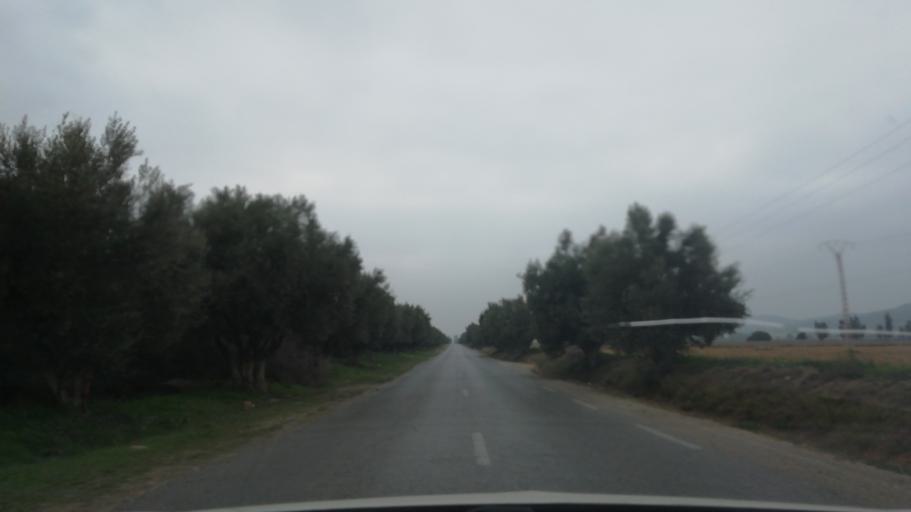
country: DZ
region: Sidi Bel Abbes
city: Sfizef
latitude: 35.2264
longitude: -0.2723
